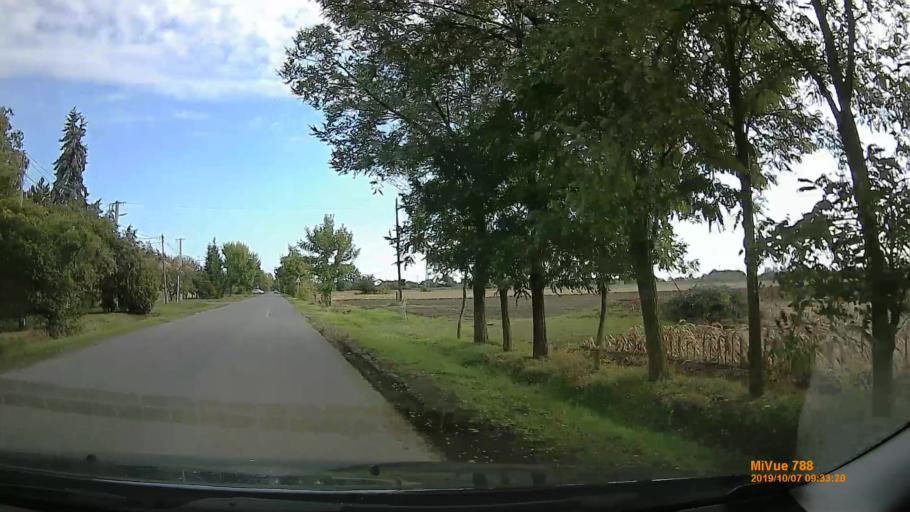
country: HU
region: Bekes
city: Szarvas
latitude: 46.8199
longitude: 20.6574
